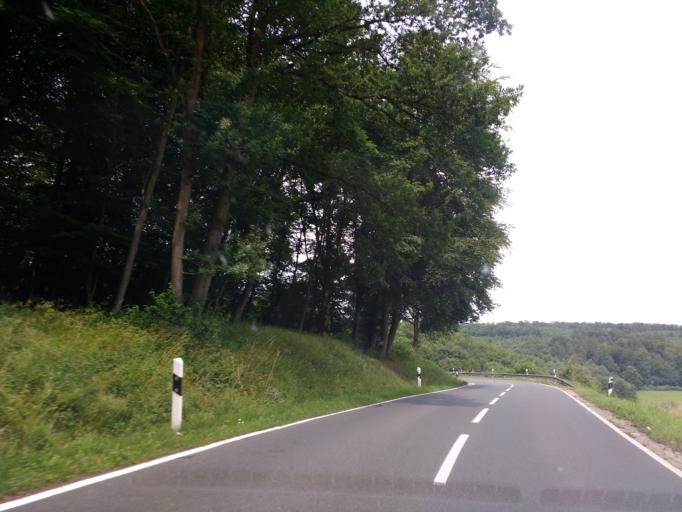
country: DE
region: Lower Saxony
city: Bad Pyrmont
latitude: 51.9960
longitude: 9.2105
